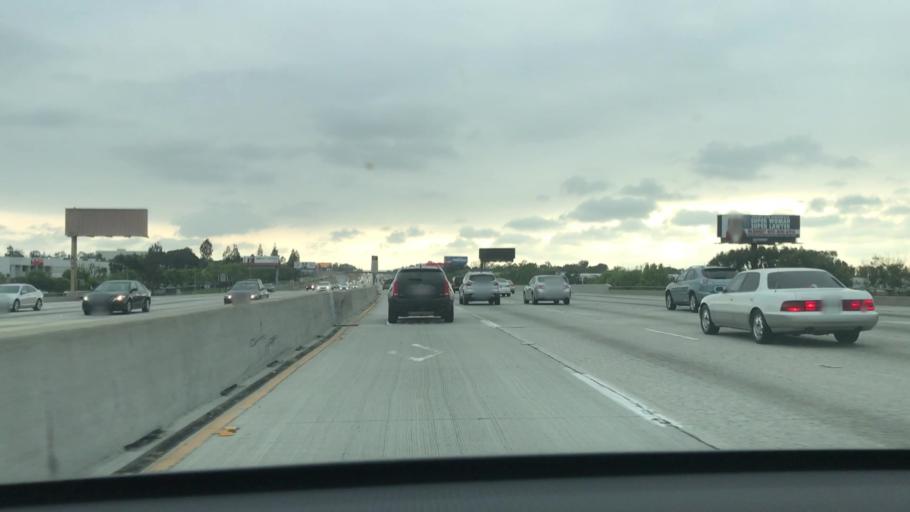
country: US
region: California
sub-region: Los Angeles County
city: Compton
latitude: 33.8741
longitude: -118.2242
